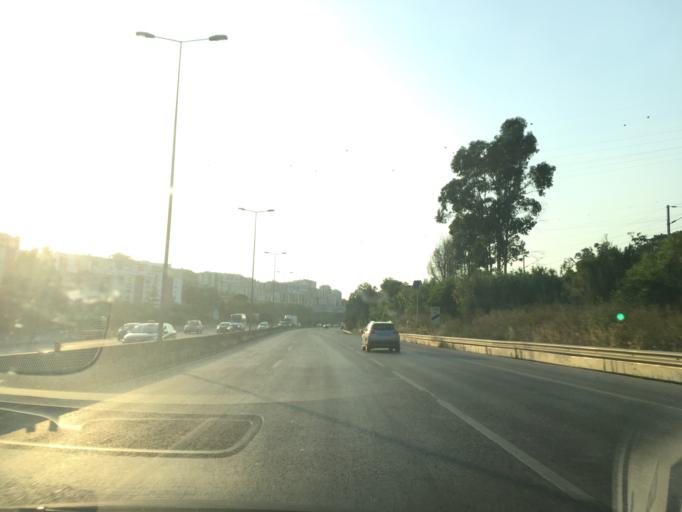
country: PT
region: Lisbon
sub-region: Sintra
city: Cacem
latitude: 38.7568
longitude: -9.2909
